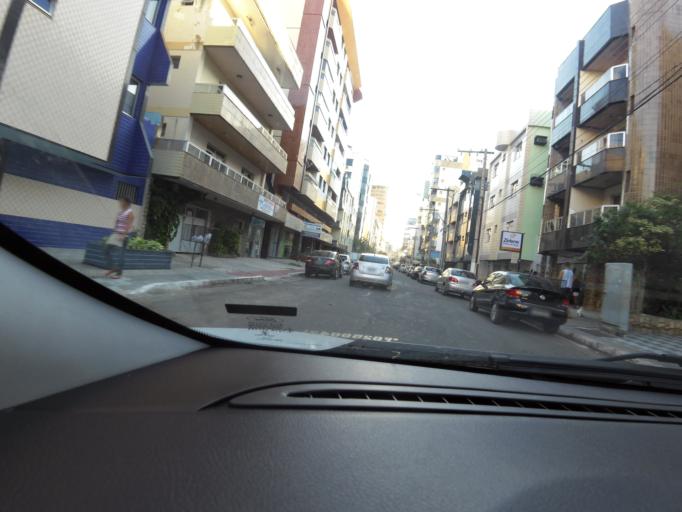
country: BR
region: Espirito Santo
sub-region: Guarapari
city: Guarapari
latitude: -20.6509
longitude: -40.4820
